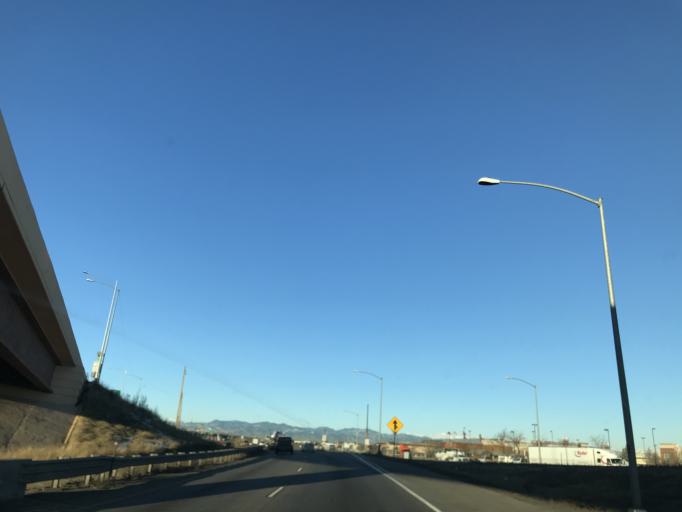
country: US
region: Colorado
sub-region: Adams County
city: Commerce City
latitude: 39.7783
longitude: -104.8871
